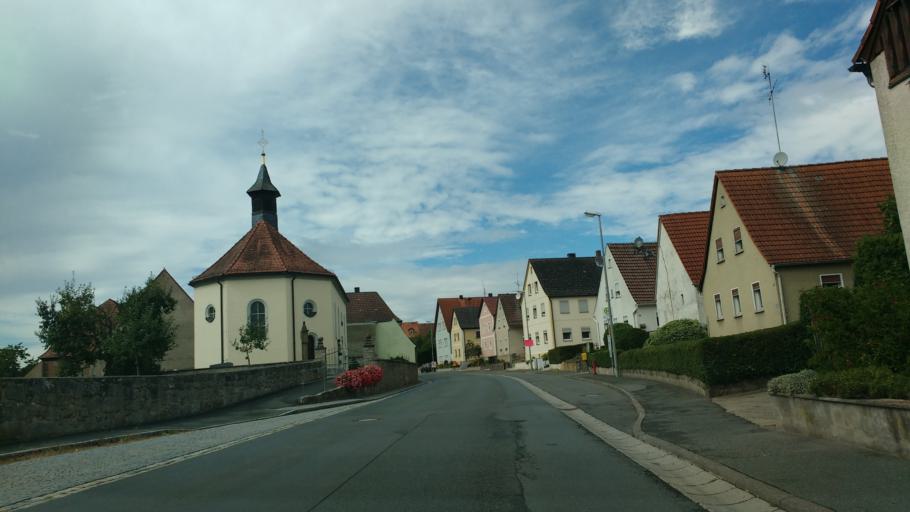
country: DE
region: Bavaria
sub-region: Upper Franconia
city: Schlusselfeld
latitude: 49.7601
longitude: 10.6091
